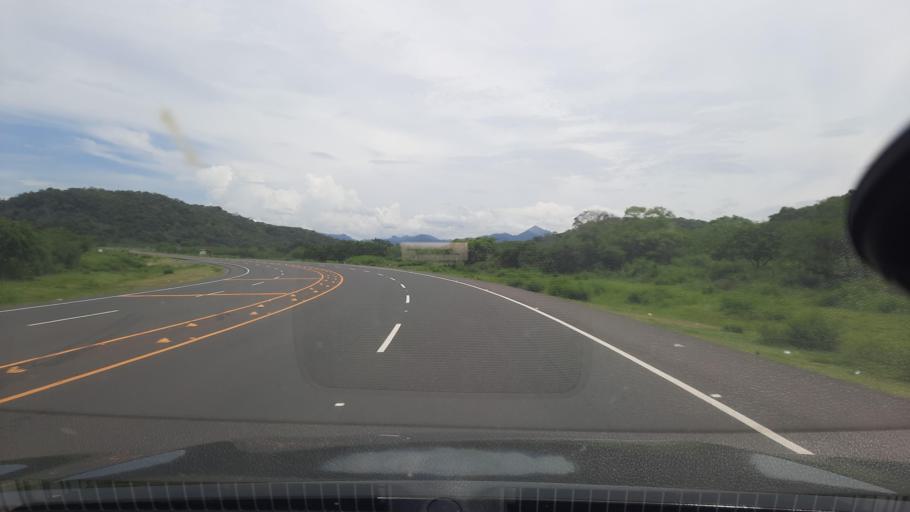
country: HN
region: Valle
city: Aramecina
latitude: 13.7268
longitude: -87.7104
